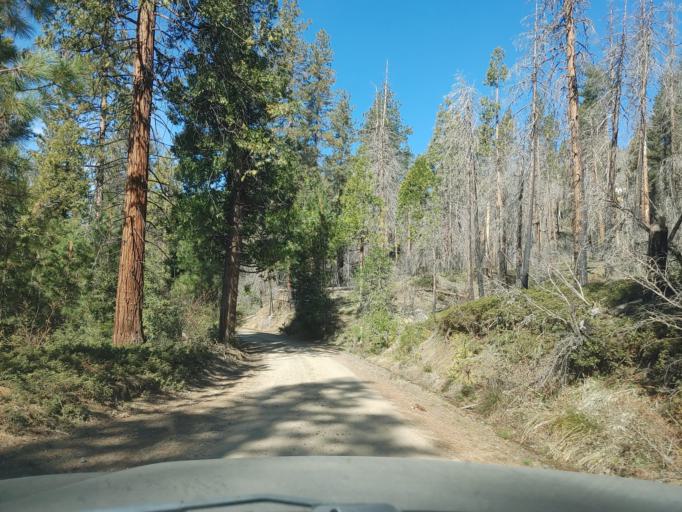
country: US
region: California
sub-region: Madera County
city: Ahwahnee
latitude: 37.4386
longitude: -119.6615
